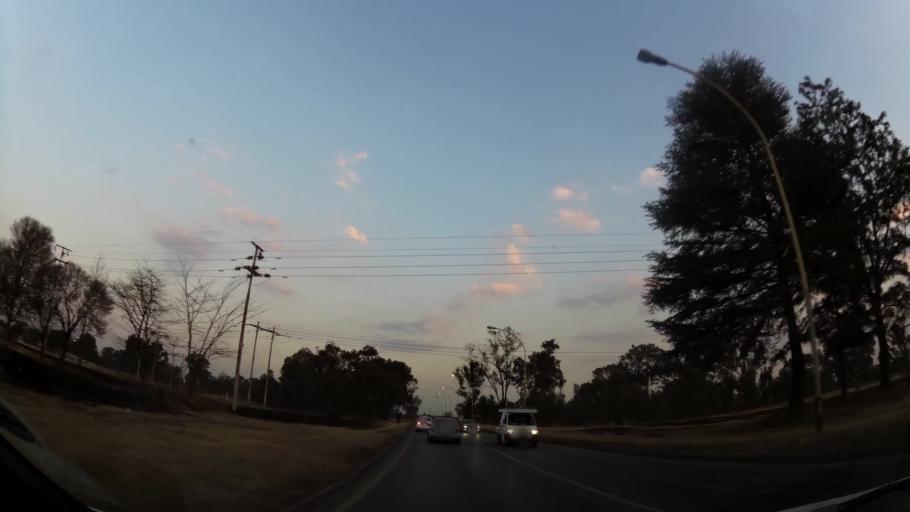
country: ZA
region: Gauteng
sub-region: Ekurhuleni Metropolitan Municipality
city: Springs
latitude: -26.2671
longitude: 28.4277
